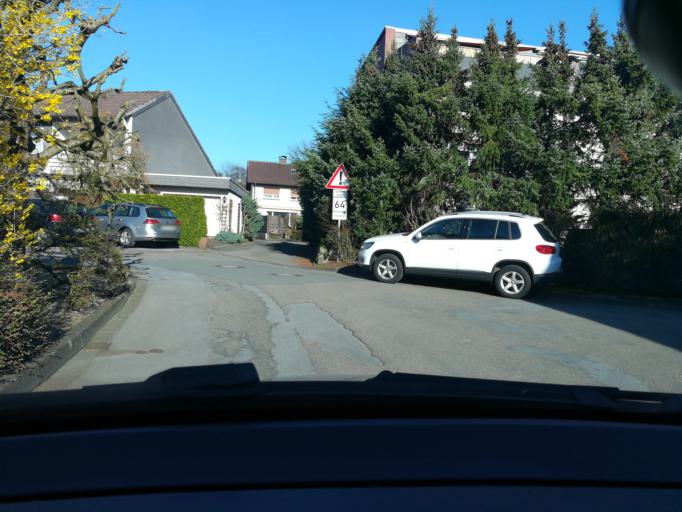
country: DE
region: North Rhine-Westphalia
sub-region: Regierungsbezirk Detmold
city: Oerlinghausen
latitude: 51.9503
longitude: 8.5975
